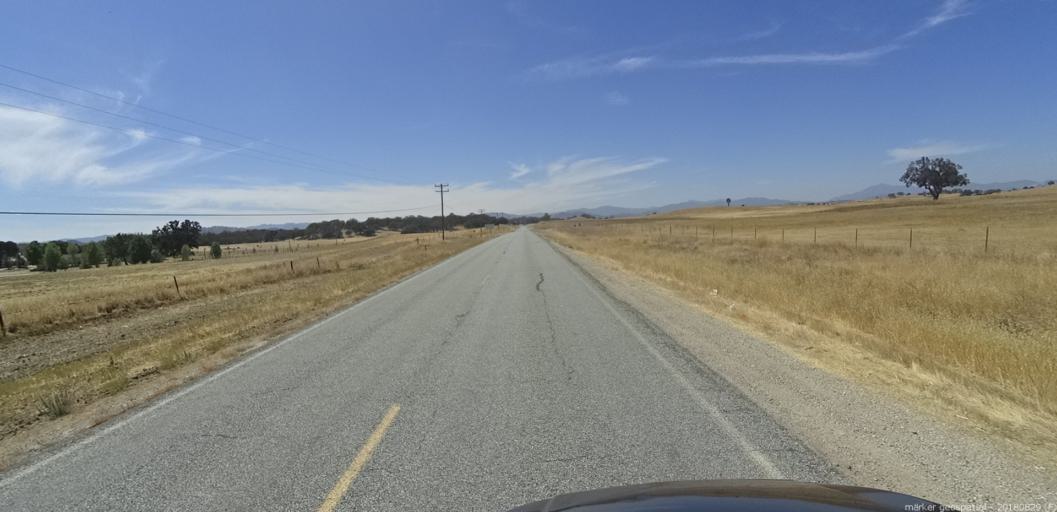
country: US
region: California
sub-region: Monterey County
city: King City
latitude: 35.9369
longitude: -121.0891
